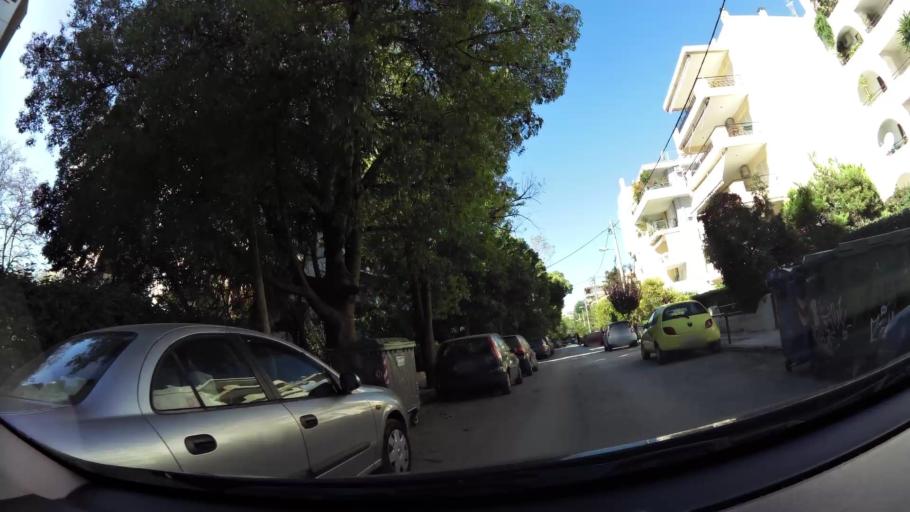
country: GR
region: Attica
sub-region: Nomarchia Athinas
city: Khalandrion
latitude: 38.0310
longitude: 23.8129
